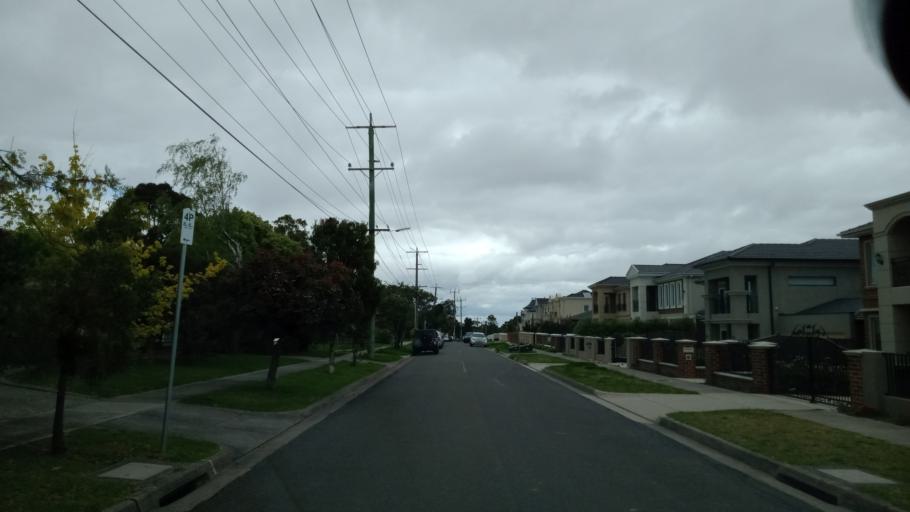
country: AU
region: Victoria
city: Burwood East
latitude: -37.8761
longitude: 145.1576
